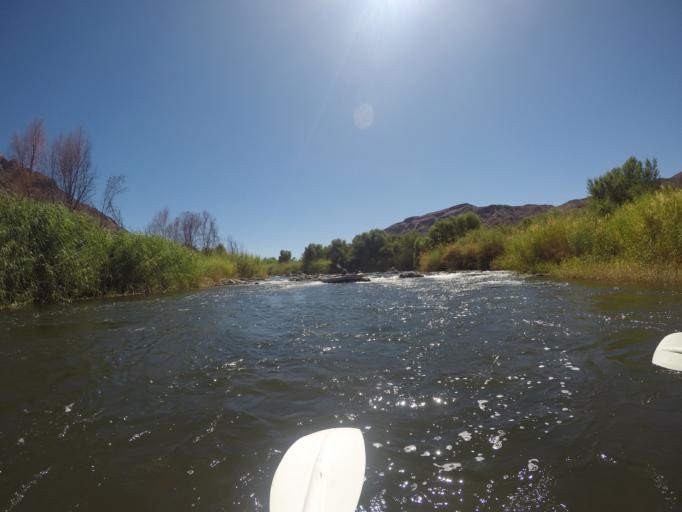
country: ZA
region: Northern Cape
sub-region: Namakwa District Municipality
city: Port Nolloth
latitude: -28.7221
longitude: 17.4308
